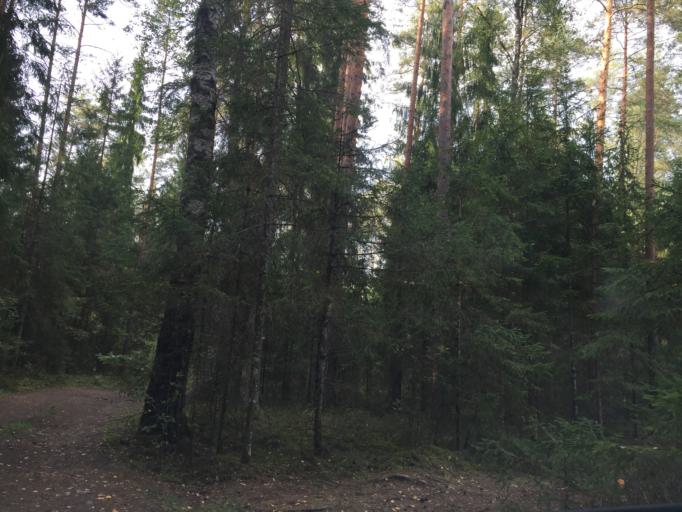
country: LV
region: Baldone
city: Baldone
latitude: 56.7841
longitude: 24.4414
